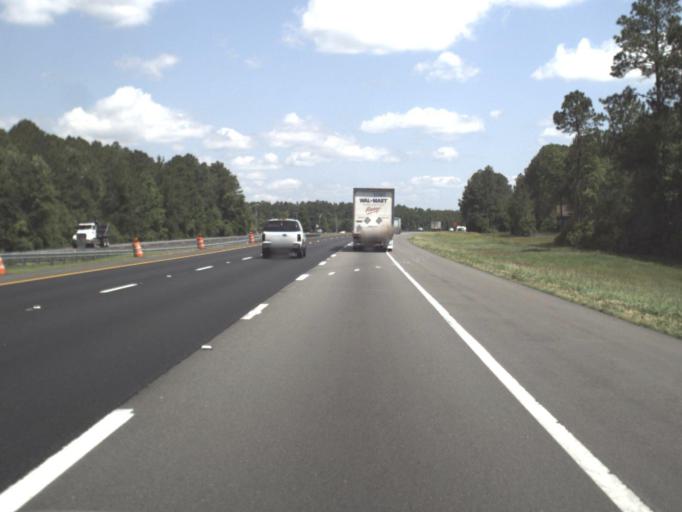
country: US
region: Florida
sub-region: Nassau County
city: Yulee
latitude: 30.6918
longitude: -81.6753
